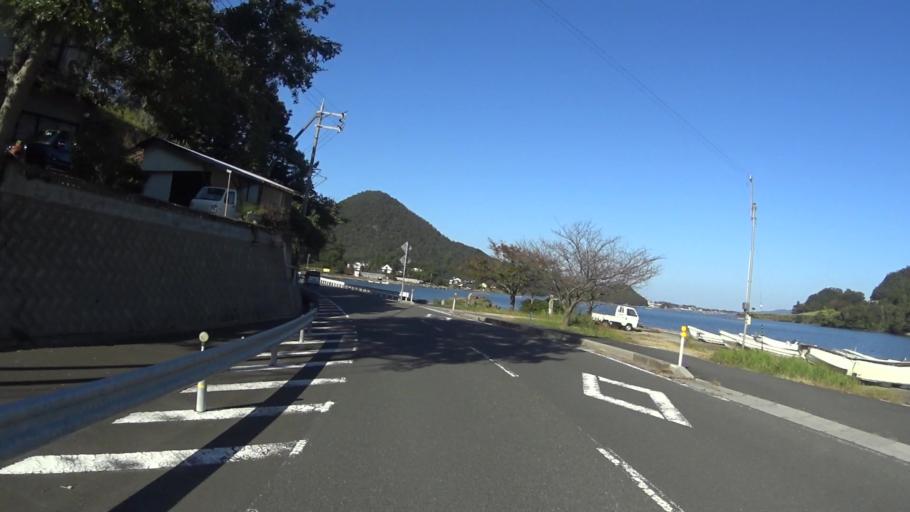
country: JP
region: Hyogo
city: Toyooka
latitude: 35.6289
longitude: 134.8876
